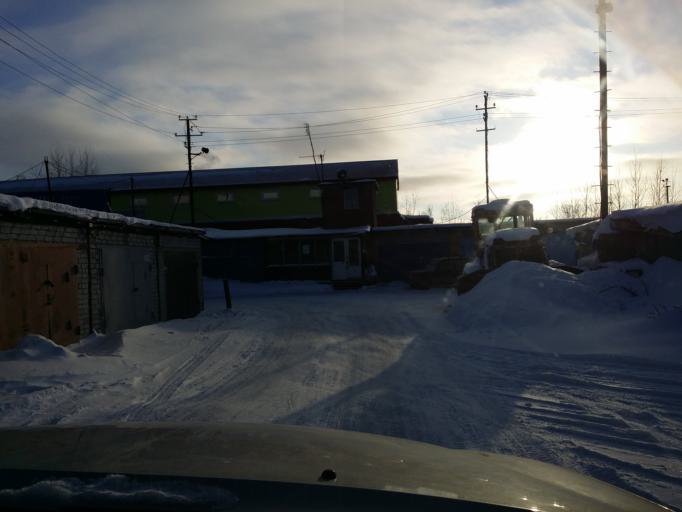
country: RU
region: Khanty-Mansiyskiy Avtonomnyy Okrug
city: Megion
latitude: 61.0439
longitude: 76.1020
